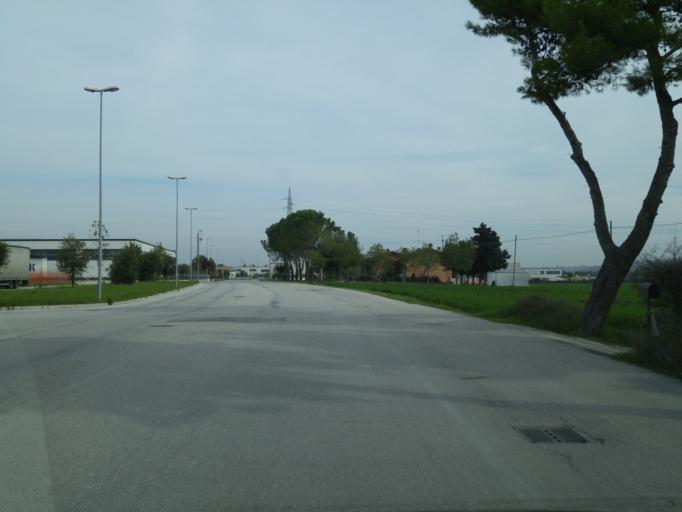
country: IT
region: The Marches
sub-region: Provincia di Pesaro e Urbino
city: Lucrezia
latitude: 43.7656
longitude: 12.9555
